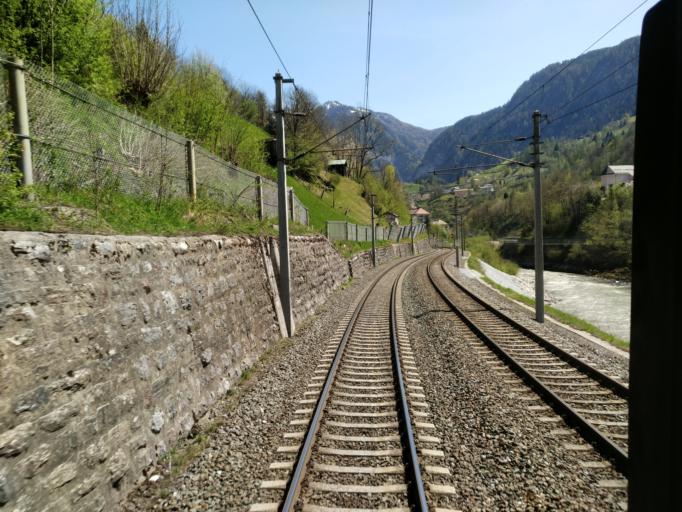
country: AT
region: Salzburg
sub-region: Politischer Bezirk Zell am See
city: Lend
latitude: 47.3014
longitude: 13.0420
